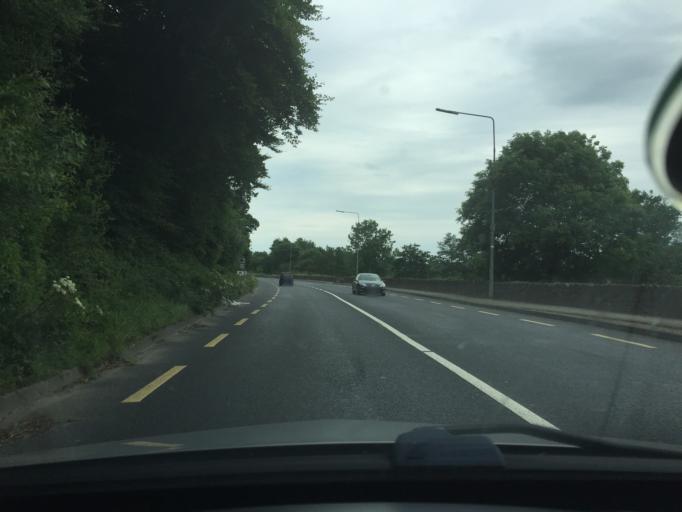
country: IE
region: Leinster
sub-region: Loch Garman
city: Enniscorthy
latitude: 52.4975
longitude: -6.5652
